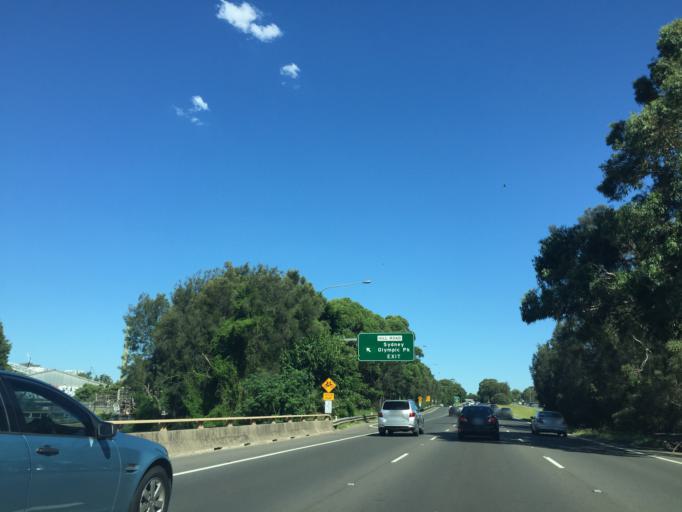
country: AU
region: New South Wales
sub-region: Auburn
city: Auburn
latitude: -33.8471
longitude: 151.0504
